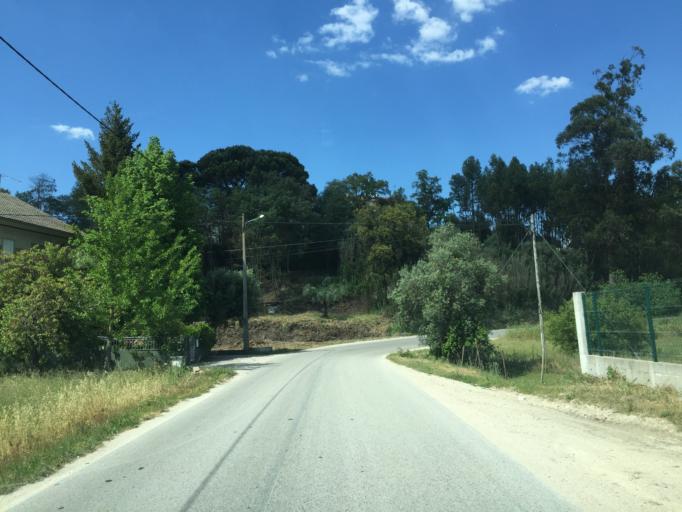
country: PT
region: Leiria
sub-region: Alvaiazere
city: Alvaiazere
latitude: 39.7577
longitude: -8.4657
